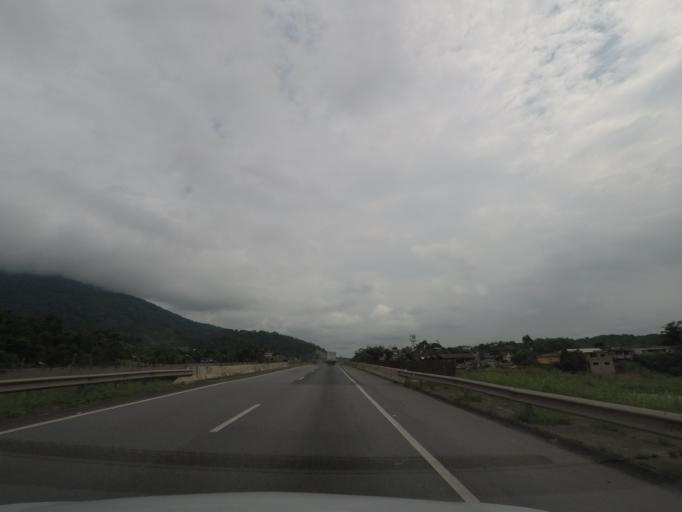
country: BR
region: Sao Paulo
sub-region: Miracatu
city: Miracatu
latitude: -24.2883
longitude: -47.4597
